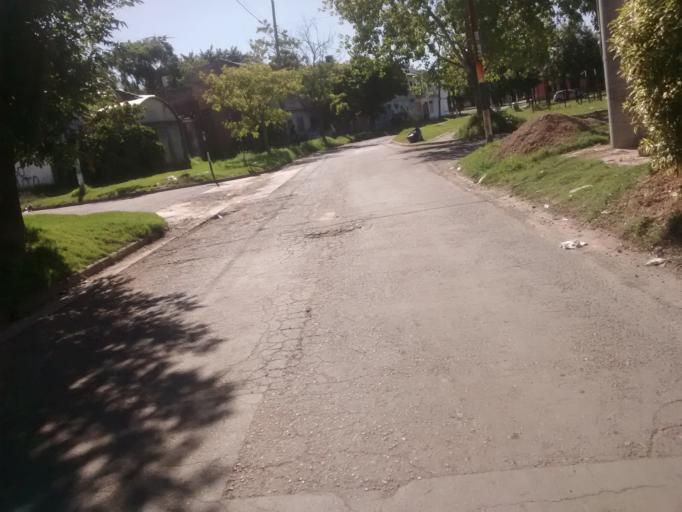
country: AR
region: Buenos Aires
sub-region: Partido de La Plata
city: La Plata
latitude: -34.9343
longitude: -57.9015
